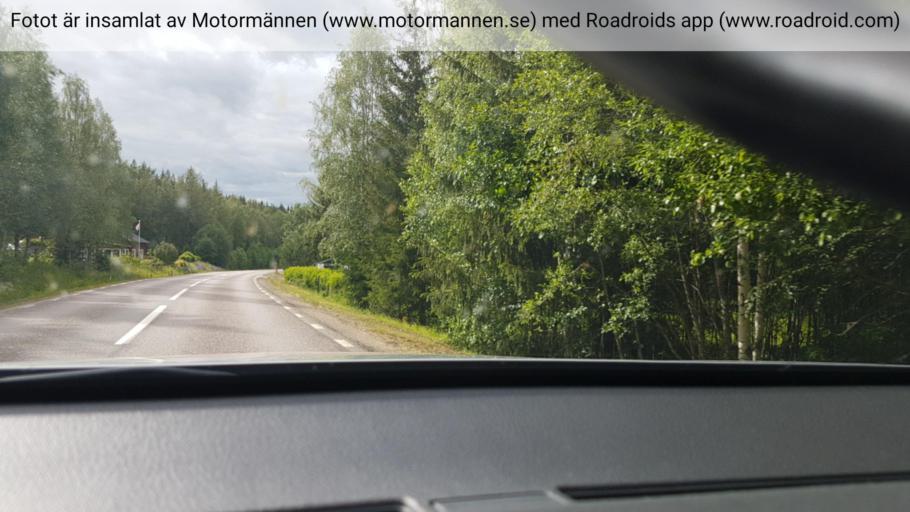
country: NO
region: Hedmark
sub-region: Trysil
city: Innbygda
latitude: 60.8998
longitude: 12.5796
